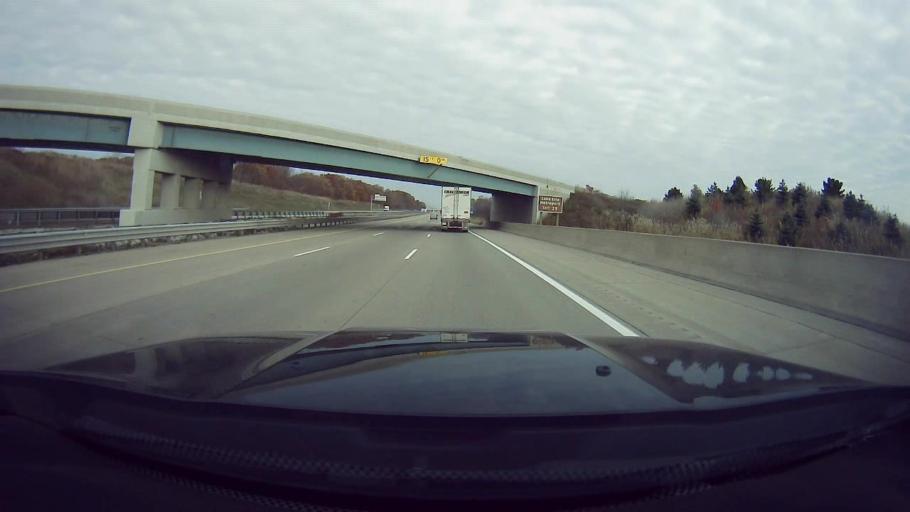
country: US
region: Michigan
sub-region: Wayne County
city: Rockwood
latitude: 42.0847
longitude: -83.2417
